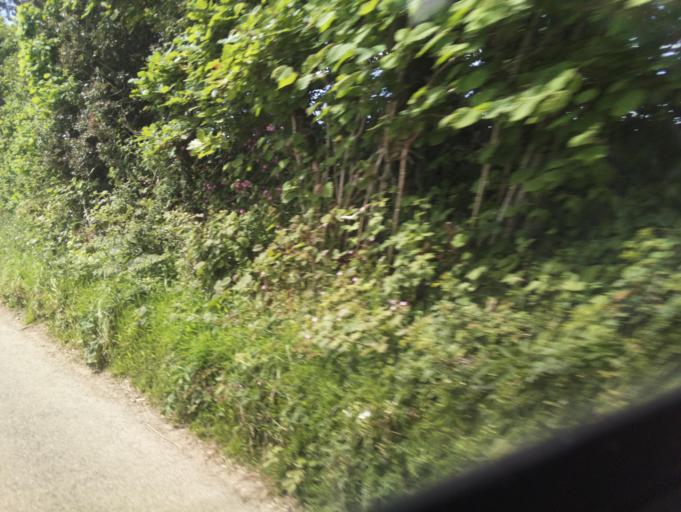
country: GB
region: England
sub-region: Devon
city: Kingsbridge
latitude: 50.3603
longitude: -3.7496
